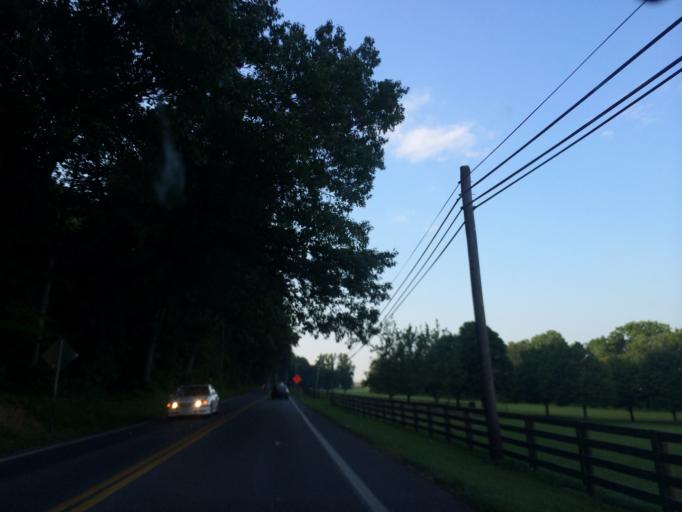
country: US
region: Maryland
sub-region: Carroll County
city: Sykesville
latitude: 39.3268
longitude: -76.8989
